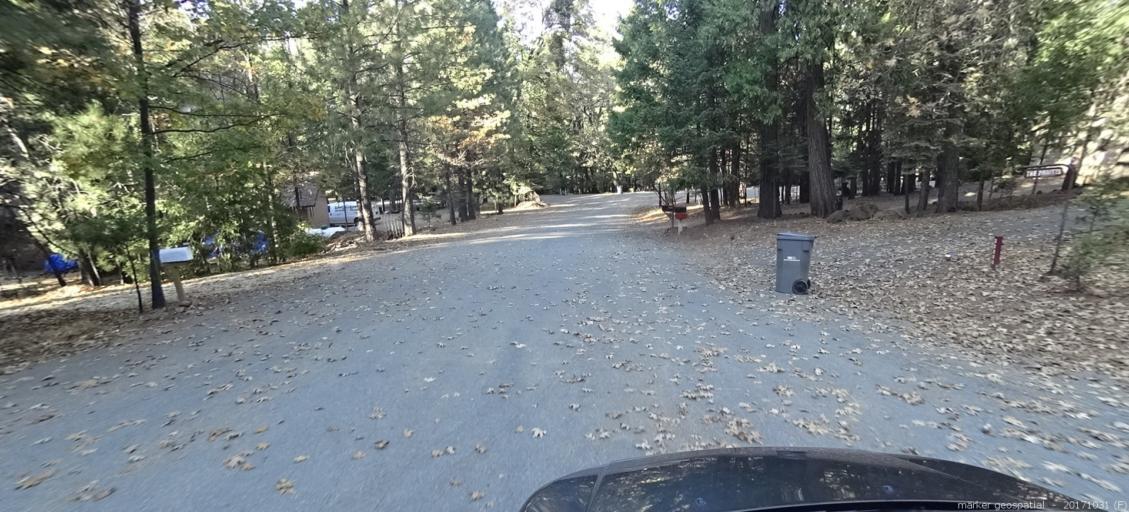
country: US
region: California
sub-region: Shasta County
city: Shingletown
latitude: 40.4989
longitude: -121.9019
